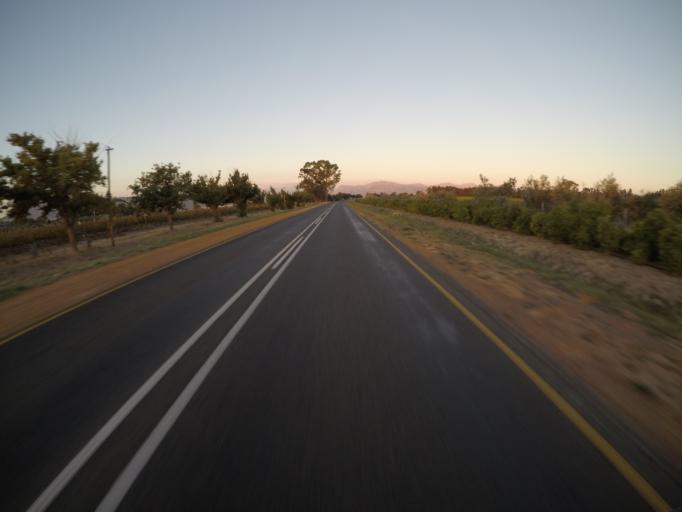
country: ZA
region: Western Cape
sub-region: Cape Winelands District Municipality
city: Paarl
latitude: -33.8039
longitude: 18.8869
